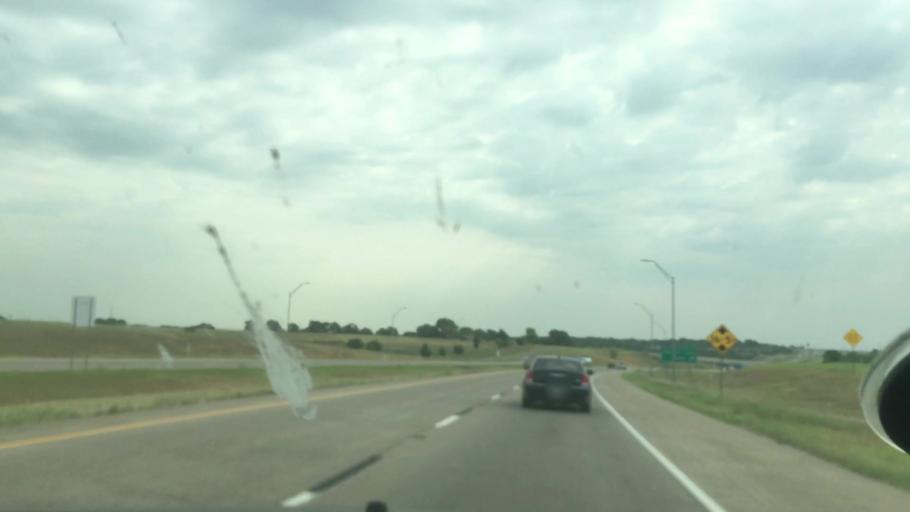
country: US
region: Texas
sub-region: Grayson County
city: Denison
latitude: 33.7861
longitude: -96.5782
